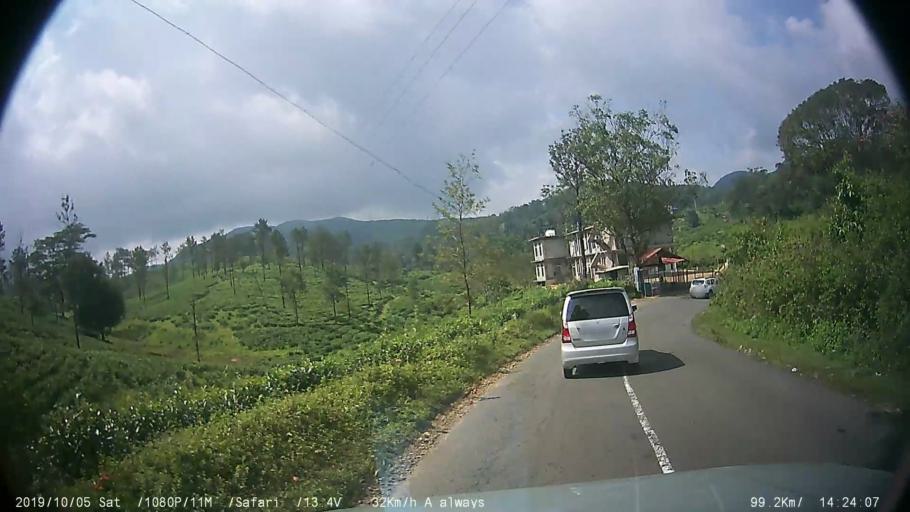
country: IN
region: Kerala
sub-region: Kottayam
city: Erattupetta
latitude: 9.5934
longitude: 76.9690
